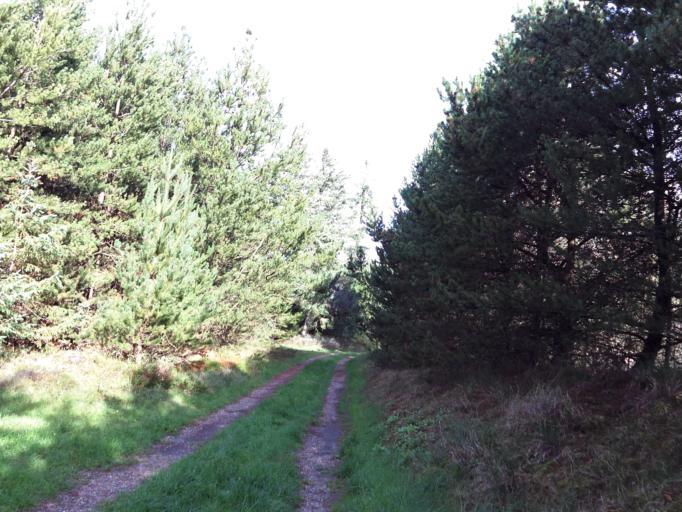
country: DK
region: South Denmark
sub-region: Varde Kommune
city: Oksbol
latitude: 55.5567
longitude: 8.2106
